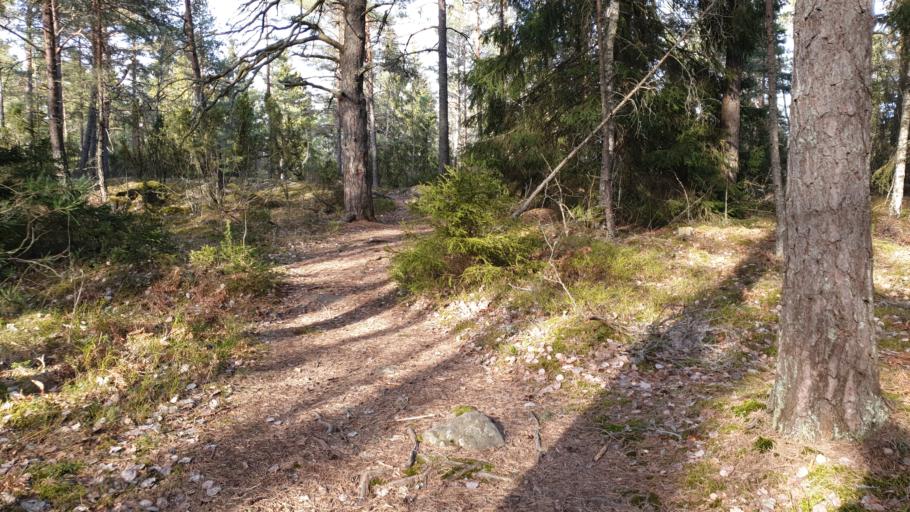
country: SE
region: Uppsala
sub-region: Enkopings Kommun
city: Grillby
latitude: 59.5982
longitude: 17.1621
